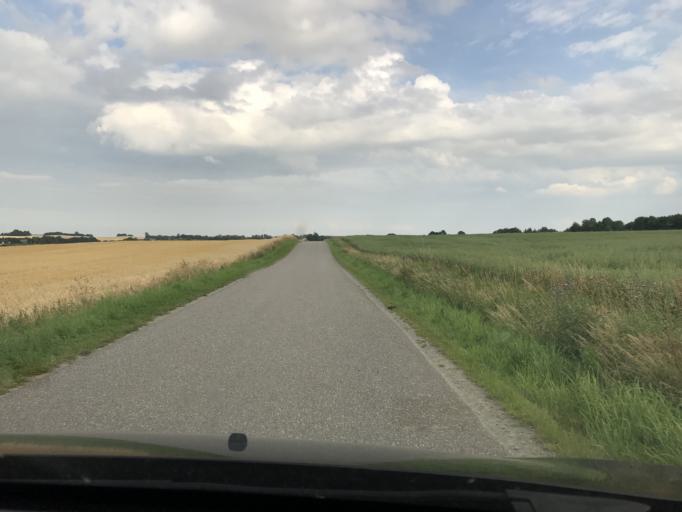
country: DK
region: South Denmark
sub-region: Vejle Kommune
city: Jelling
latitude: 55.8039
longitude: 9.4406
